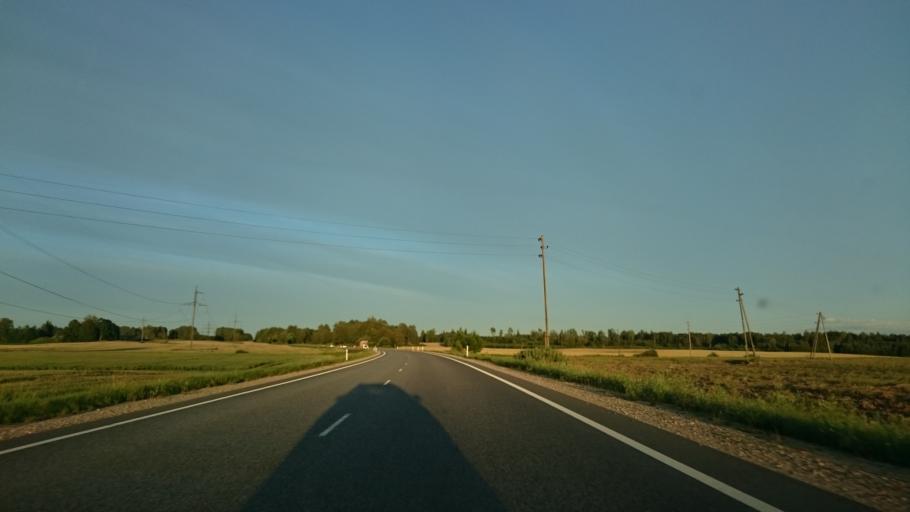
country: LV
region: Broceni
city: Broceni
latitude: 56.6633
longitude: 22.6013
